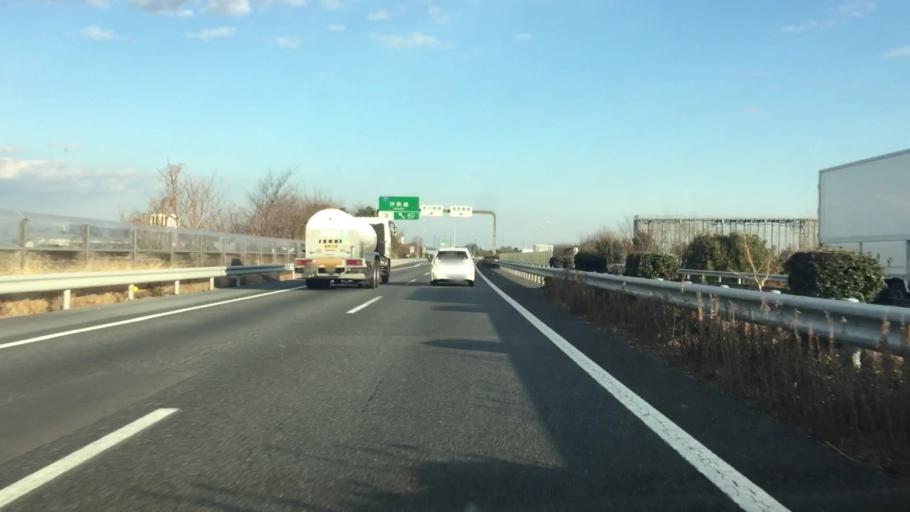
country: JP
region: Gunma
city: Isesaki
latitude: 36.3555
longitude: 139.2145
